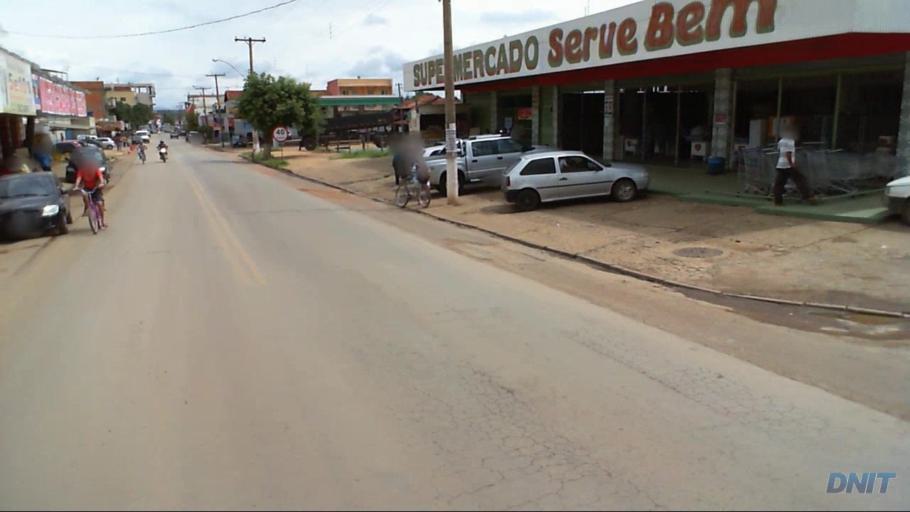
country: BR
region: Goias
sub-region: Padre Bernardo
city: Padre Bernardo
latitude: -15.1704
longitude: -48.2852
